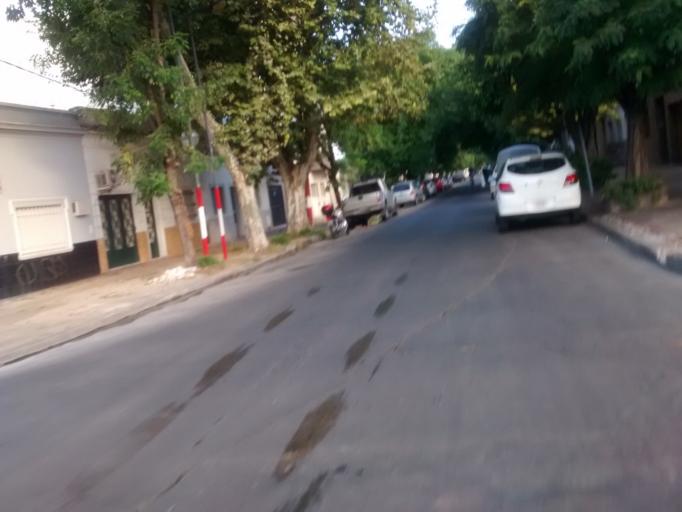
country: AR
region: Buenos Aires
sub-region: Partido de La Plata
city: La Plata
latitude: -34.9158
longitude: -57.9690
